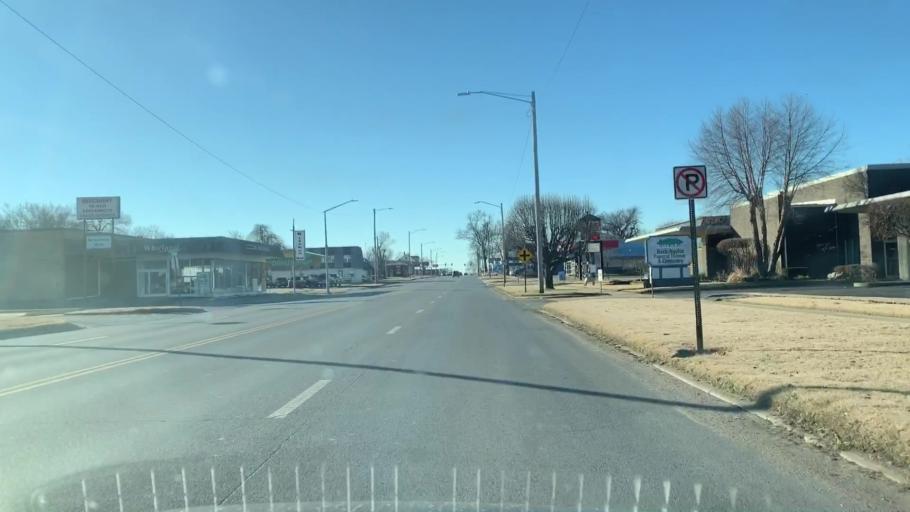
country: US
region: Kansas
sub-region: Crawford County
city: Pittsburg
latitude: 37.4041
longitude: -94.7050
